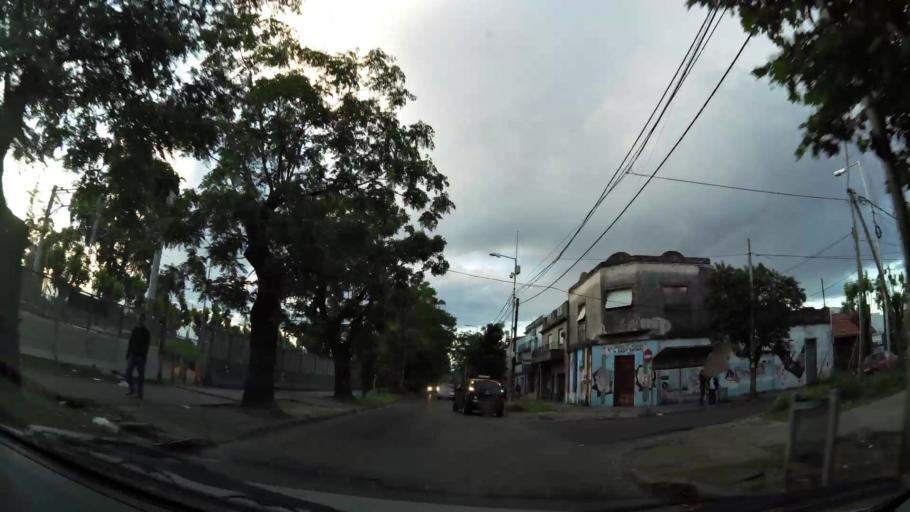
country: AR
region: Buenos Aires
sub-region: Partido de Avellaneda
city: Avellaneda
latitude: -34.6920
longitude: -58.3244
